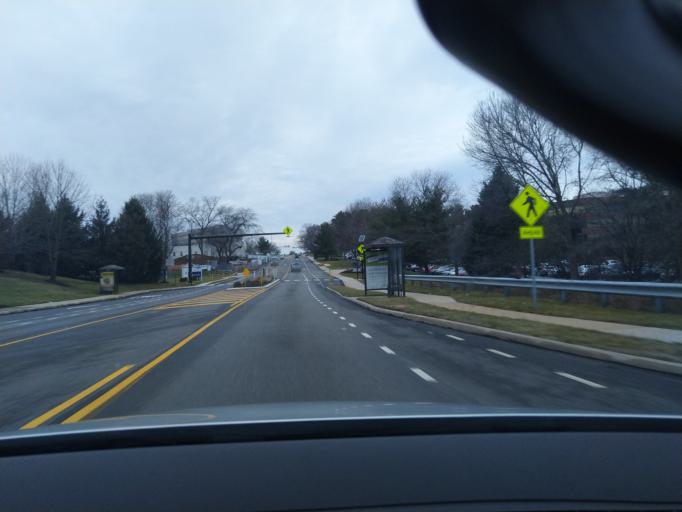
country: US
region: Pennsylvania
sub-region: Montgomery County
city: King of Prussia
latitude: 40.0951
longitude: -75.4060
